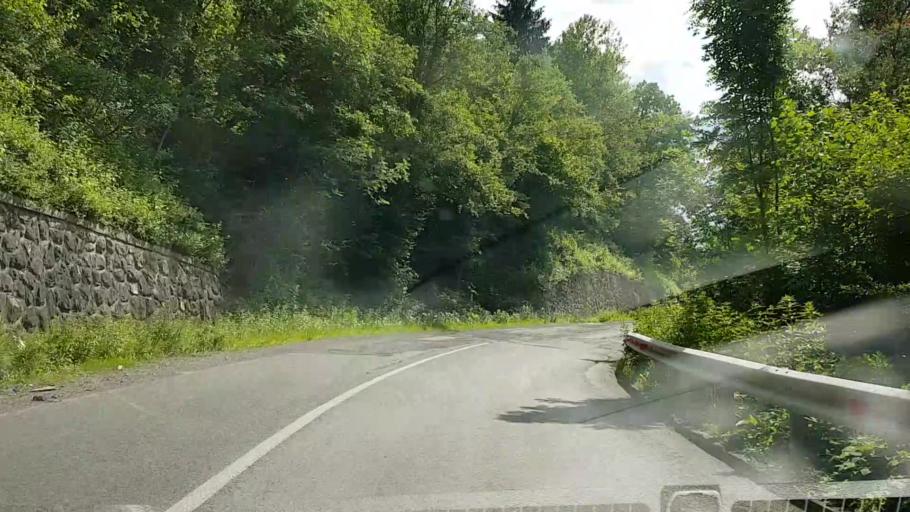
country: RO
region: Neamt
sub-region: Comuna Poiana Teiului
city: Poiana Teiului
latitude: 47.0772
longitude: 25.9660
